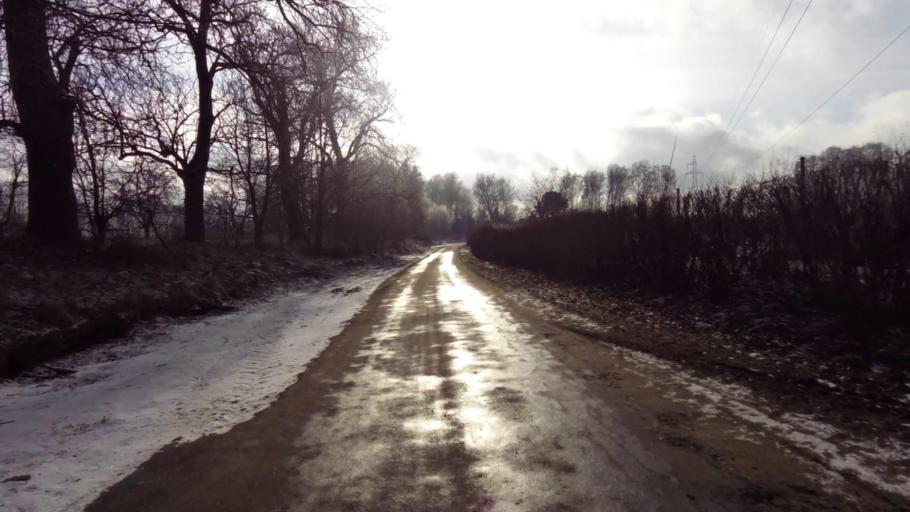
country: PL
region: West Pomeranian Voivodeship
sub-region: Powiat drawski
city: Zlocieniec
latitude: 53.5456
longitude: 16.0176
